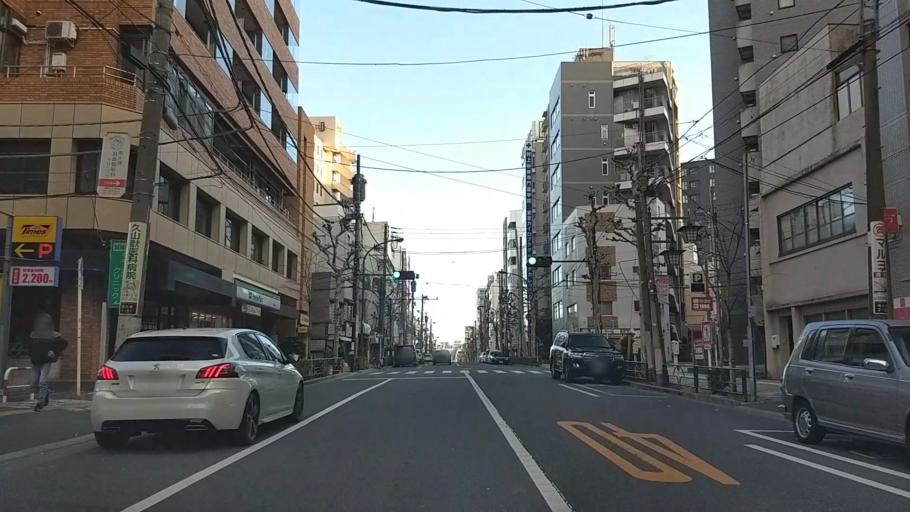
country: JP
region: Tokyo
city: Tokyo
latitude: 35.7297
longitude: 139.7308
